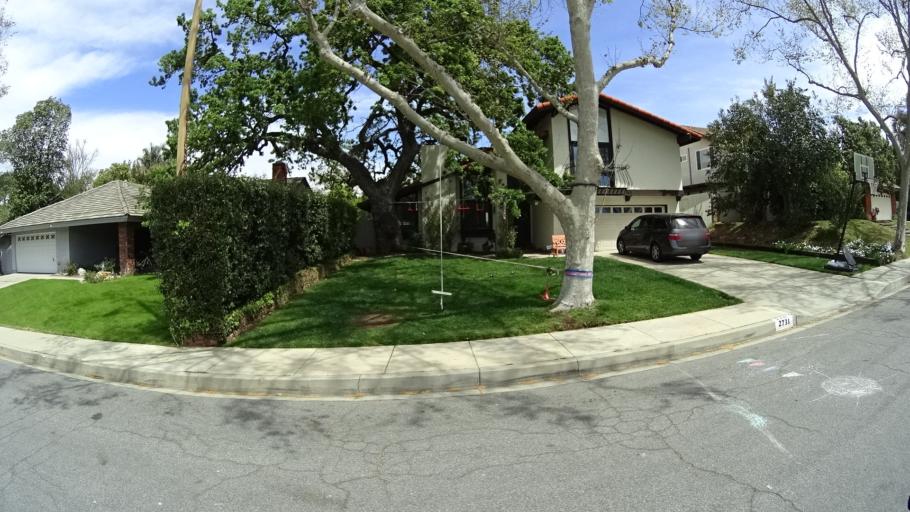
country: US
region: California
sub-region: Ventura County
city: Thousand Oaks
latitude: 34.1665
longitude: -118.8276
